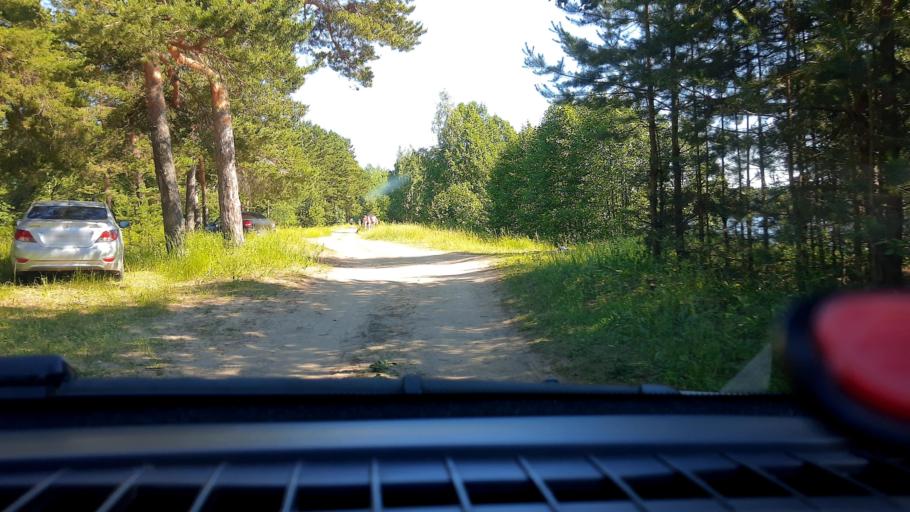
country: RU
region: Nizjnij Novgorod
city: Gidrotorf
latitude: 56.5046
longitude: 43.5389
